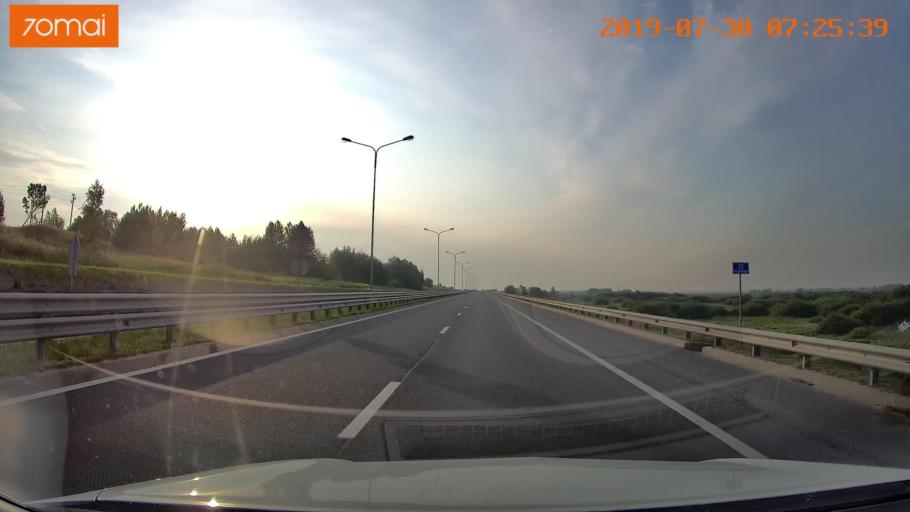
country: RU
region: Kaliningrad
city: Gvardeysk
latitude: 54.6857
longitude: 20.8399
